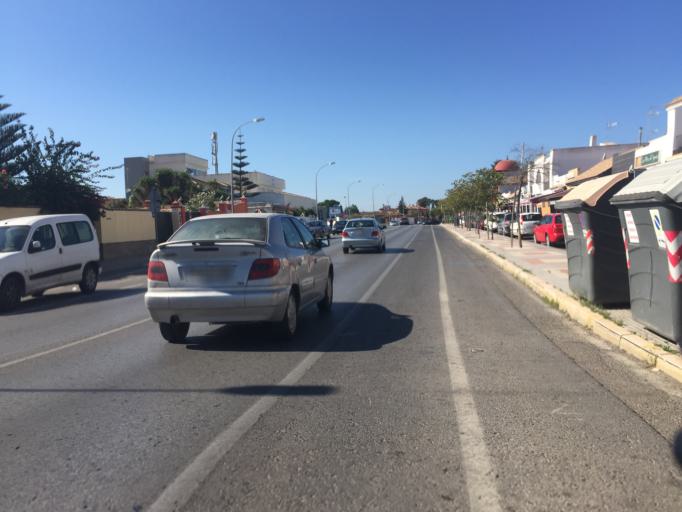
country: ES
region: Andalusia
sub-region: Provincia de Cadiz
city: Chiclana de la Frontera
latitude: 36.3957
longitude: -6.1735
